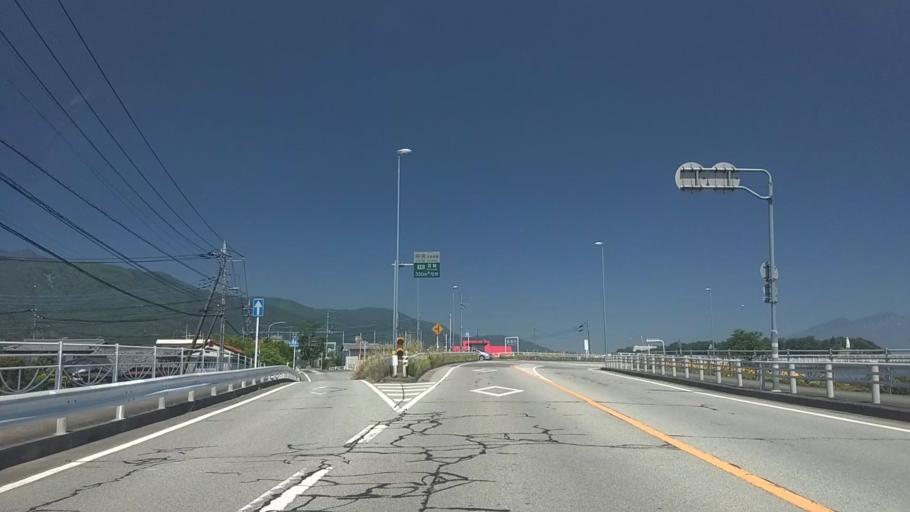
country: JP
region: Yamanashi
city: Nirasaki
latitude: 35.6984
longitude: 138.4542
